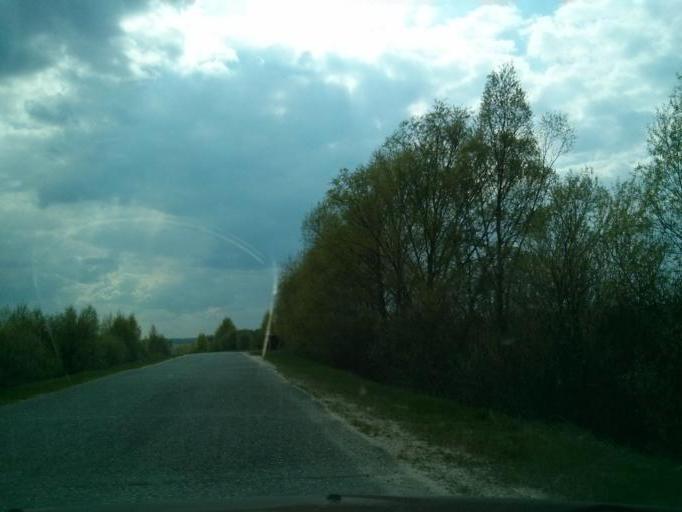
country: RU
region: Nizjnij Novgorod
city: Shimorskoye
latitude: 55.3794
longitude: 41.9351
